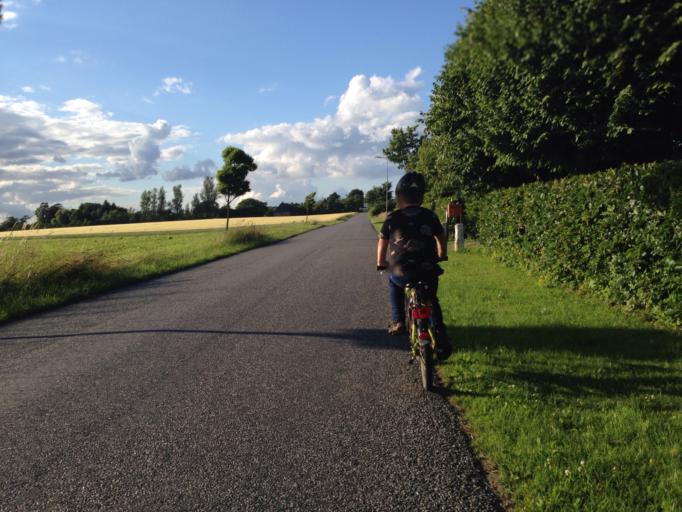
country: DK
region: South Denmark
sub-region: Middelfart Kommune
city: Norre Aby
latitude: 55.4758
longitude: 9.9034
